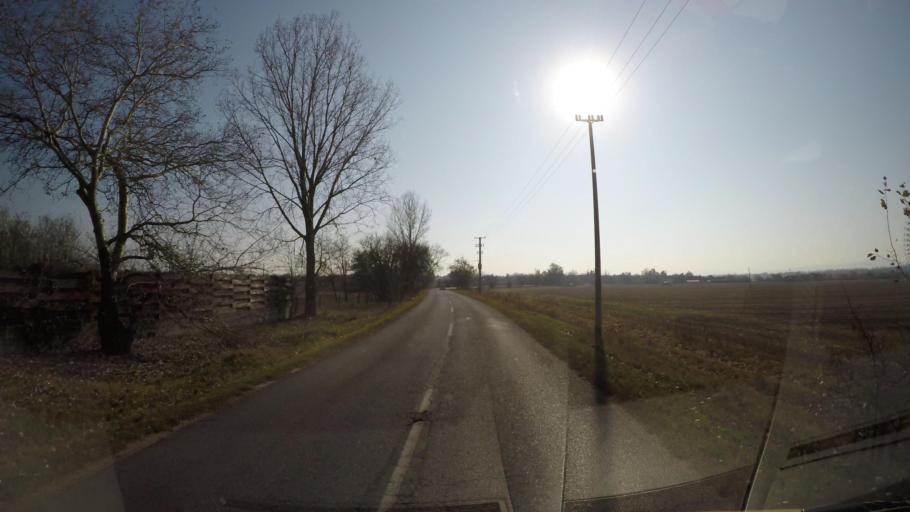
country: HU
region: Pest
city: Leanyfalu
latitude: 47.6967
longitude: 19.1040
